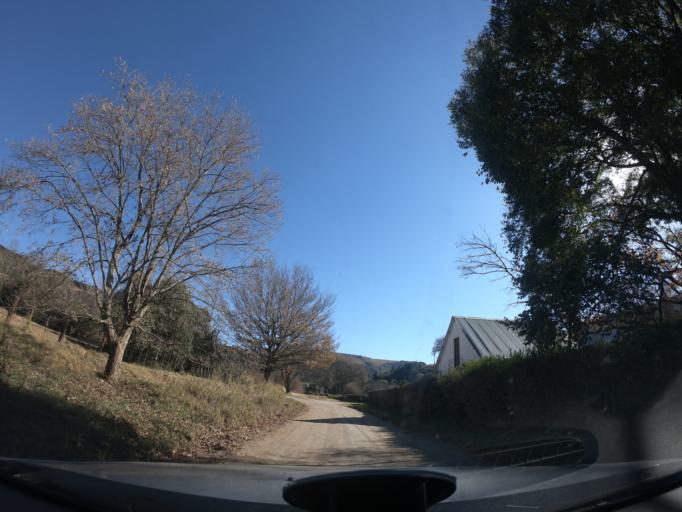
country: ZA
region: KwaZulu-Natal
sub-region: uMgungundlovu District Municipality
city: Impendle
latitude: -29.4191
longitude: 29.9059
